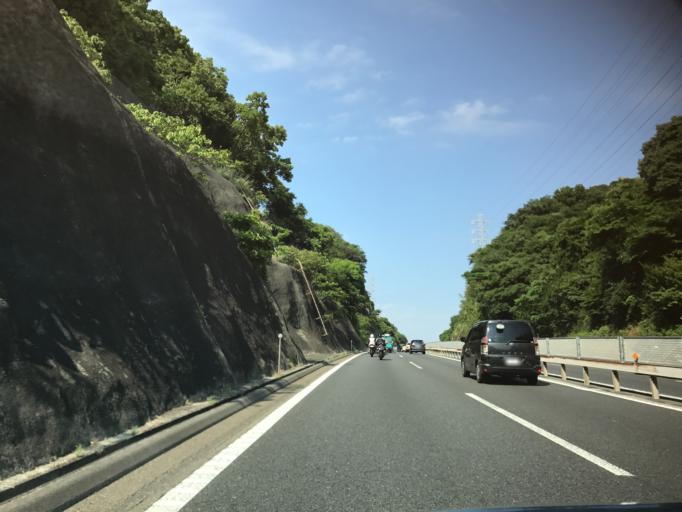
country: JP
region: Kanagawa
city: Oiso
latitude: 35.3258
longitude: 139.2831
